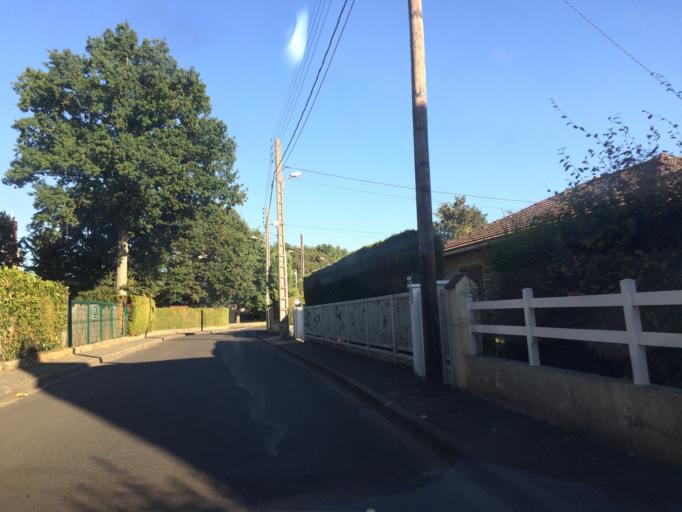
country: FR
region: Ile-de-France
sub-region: Departement de l'Essonne
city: Marolles-en-Hurepoix
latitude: 48.5653
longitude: 2.2962
